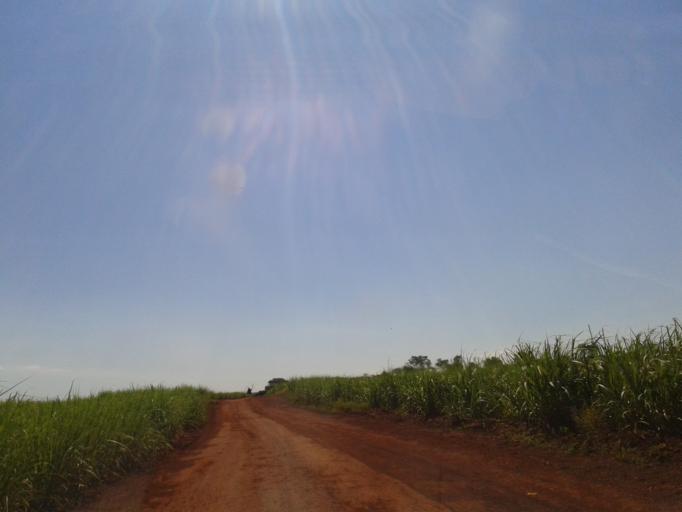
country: BR
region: Minas Gerais
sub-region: Centralina
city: Centralina
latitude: -18.6212
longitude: -49.2713
